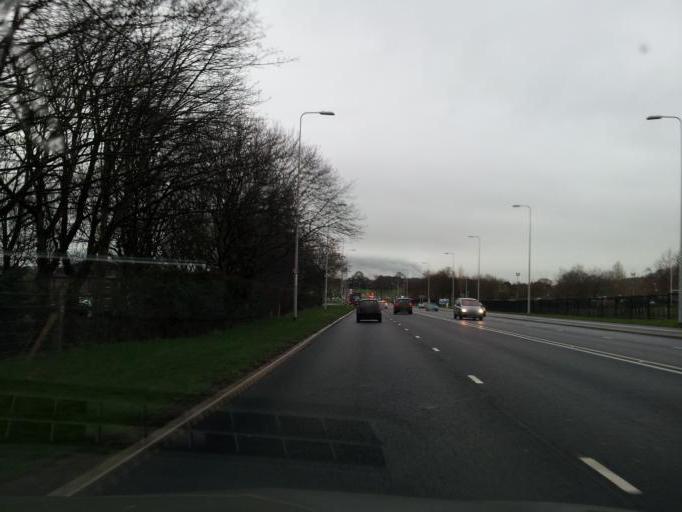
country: GB
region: England
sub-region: Nottinghamshire
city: Ruddington
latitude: 52.9100
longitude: -1.1834
